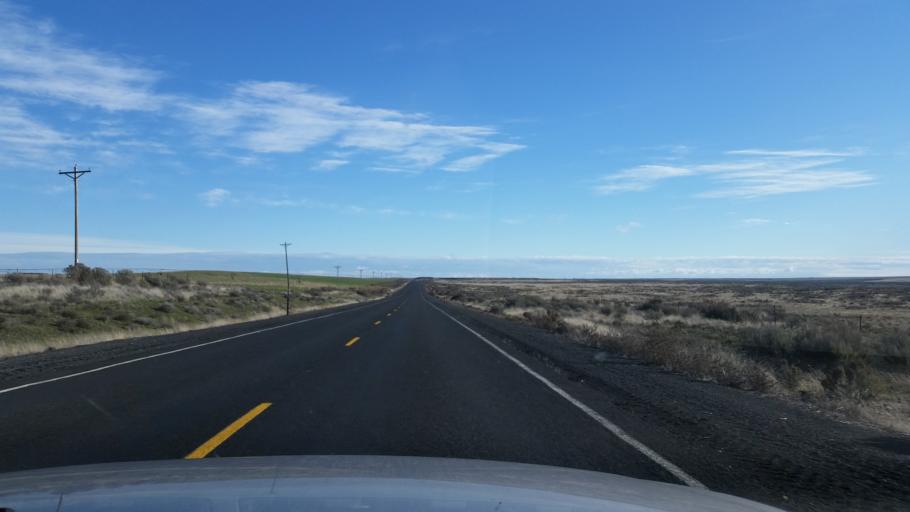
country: US
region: Washington
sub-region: Grant County
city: Warden
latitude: 47.3381
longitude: -118.9008
